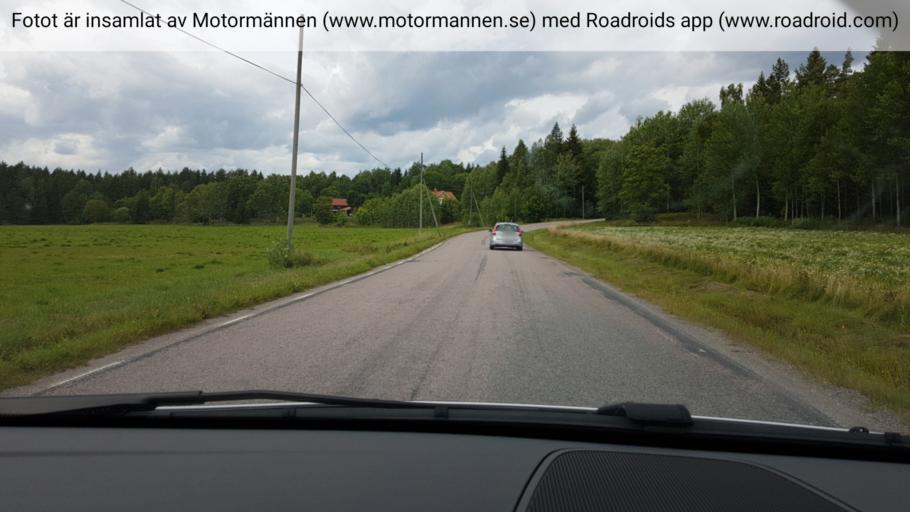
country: SE
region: Uppsala
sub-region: Osthammars Kommun
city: Gimo
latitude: 59.9695
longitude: 18.0719
